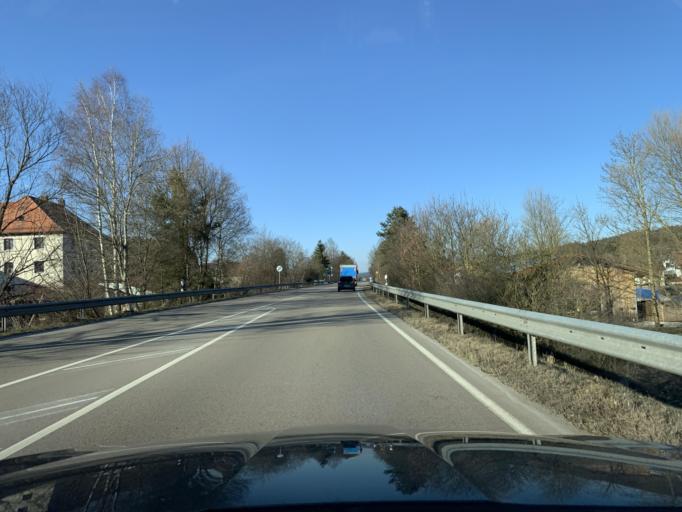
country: DE
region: Bavaria
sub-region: Upper Palatinate
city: Pemfling
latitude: 49.3015
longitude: 12.6290
